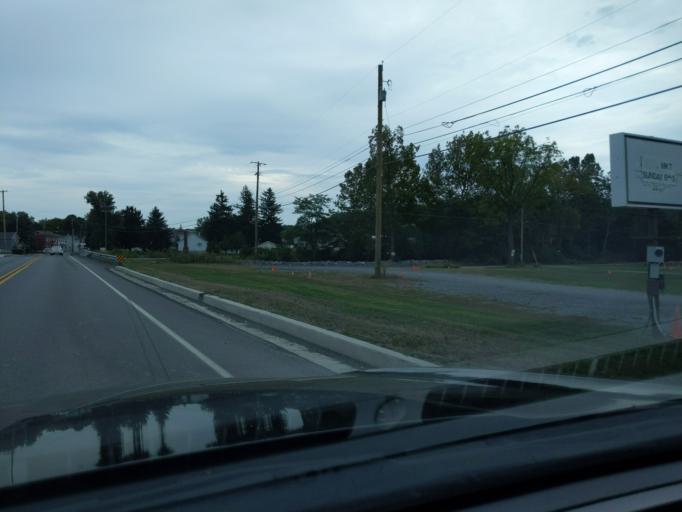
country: US
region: Pennsylvania
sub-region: Blair County
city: Duncansville
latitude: 40.3893
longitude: -78.4350
